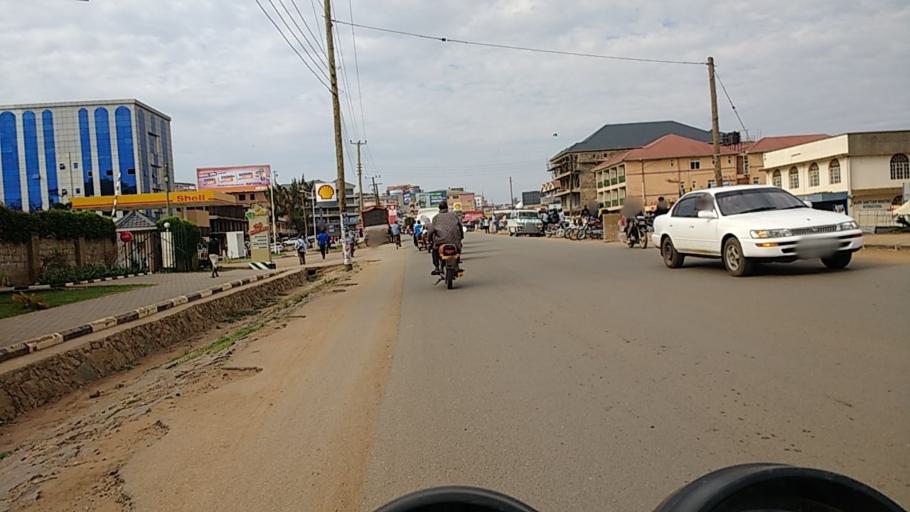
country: UG
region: Western Region
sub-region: Mbarara District
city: Mbarara
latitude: -0.6002
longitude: 30.6637
